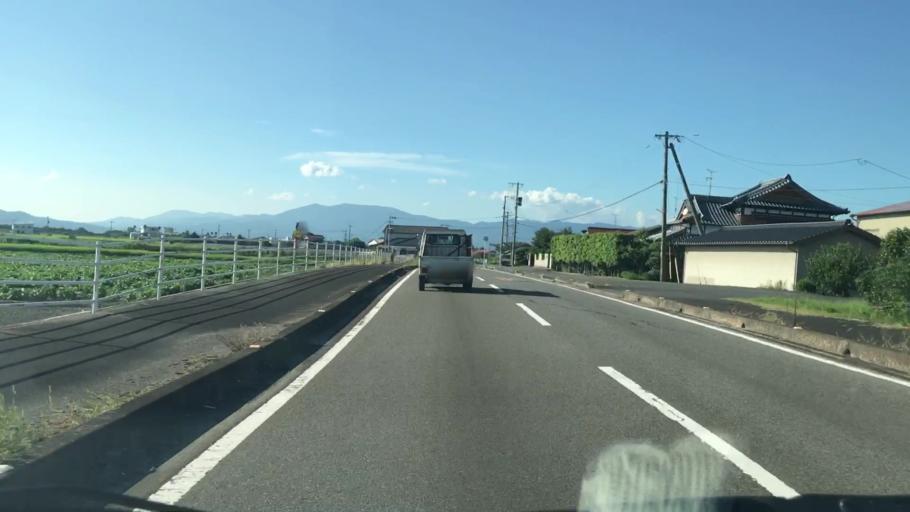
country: JP
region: Saga Prefecture
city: Saga-shi
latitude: 33.2000
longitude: 130.2666
